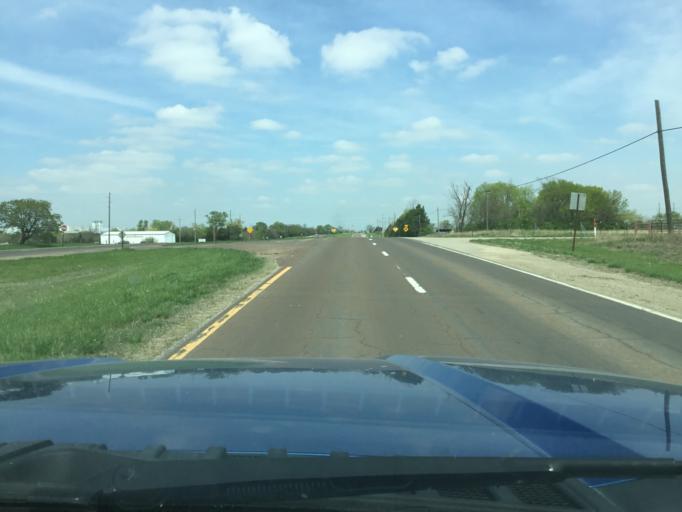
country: US
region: Kansas
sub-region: Osage County
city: Carbondale
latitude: 38.9253
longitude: -95.6875
